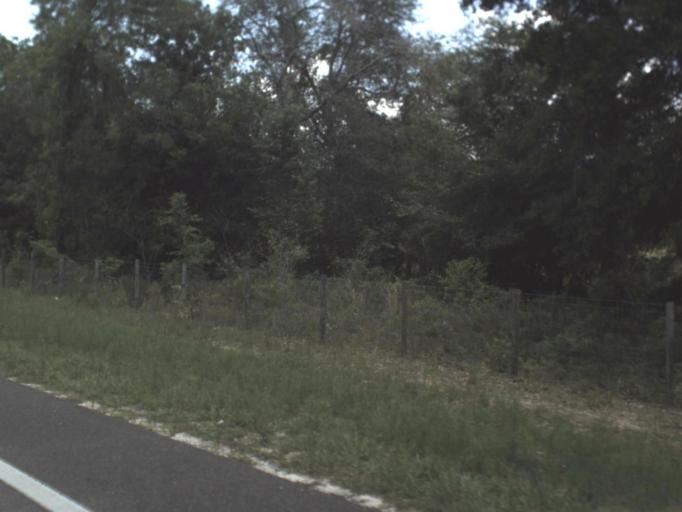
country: US
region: Florida
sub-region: Levy County
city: East Bronson
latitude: 29.4976
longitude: -82.5807
